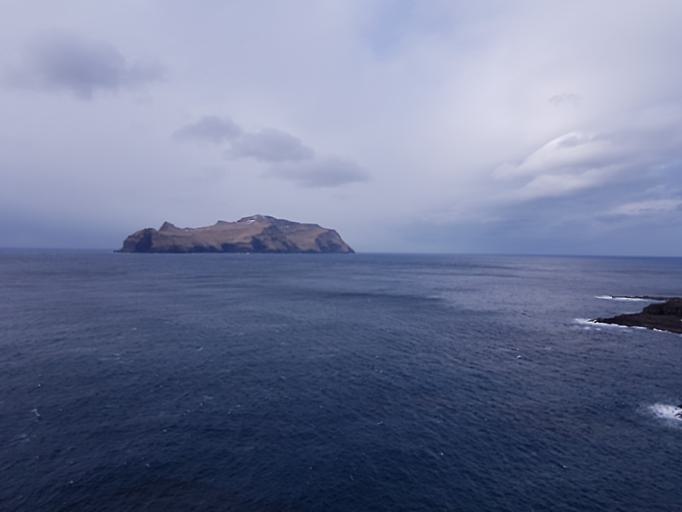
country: FO
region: Vagar
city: Sorvagur
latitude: 62.1059
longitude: -7.4349
